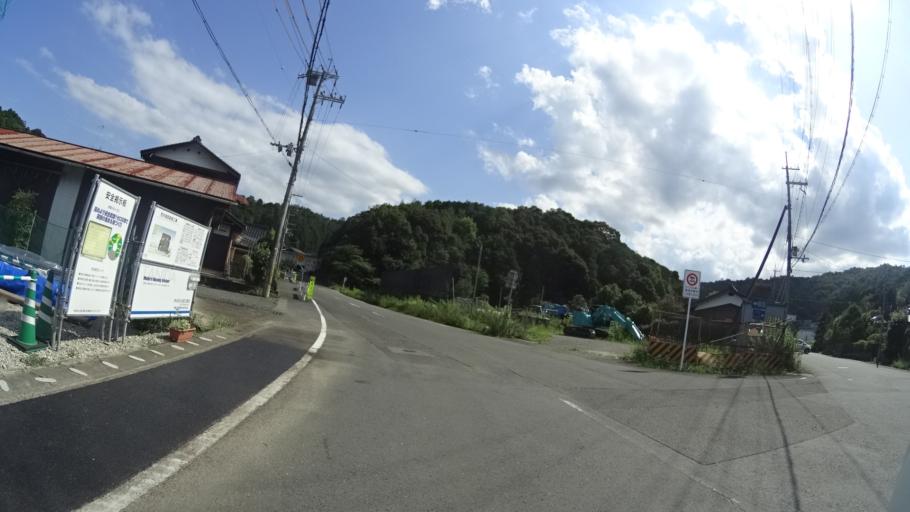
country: JP
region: Kyoto
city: Maizuru
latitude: 35.4418
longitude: 135.2954
